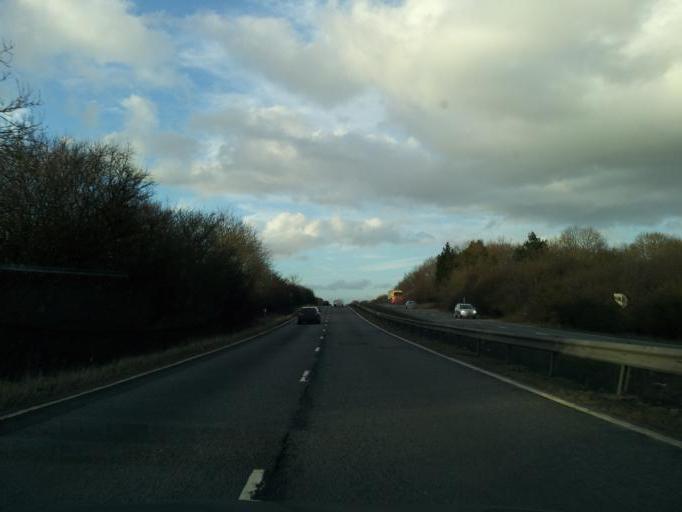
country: GB
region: England
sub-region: District of Rutland
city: Clipsham
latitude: 52.7923
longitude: -0.6107
